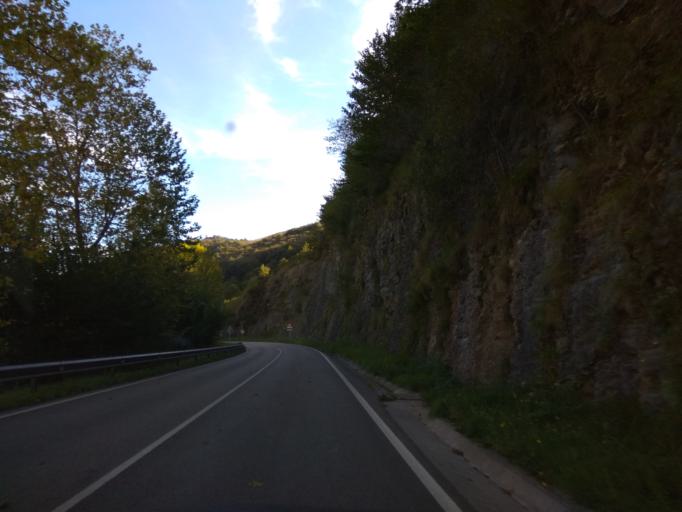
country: ES
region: Cantabria
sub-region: Provincia de Cantabria
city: Ruente
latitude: 43.2213
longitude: -4.3859
